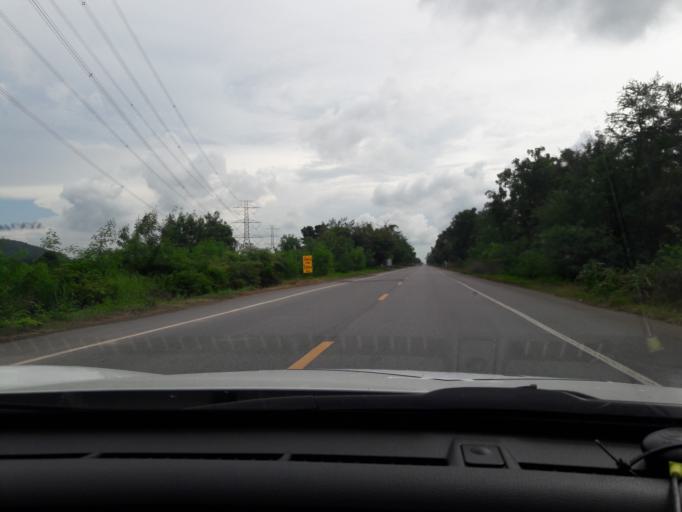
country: TH
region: Nakhon Sawan
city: Tak Fa
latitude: 15.4073
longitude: 100.5130
